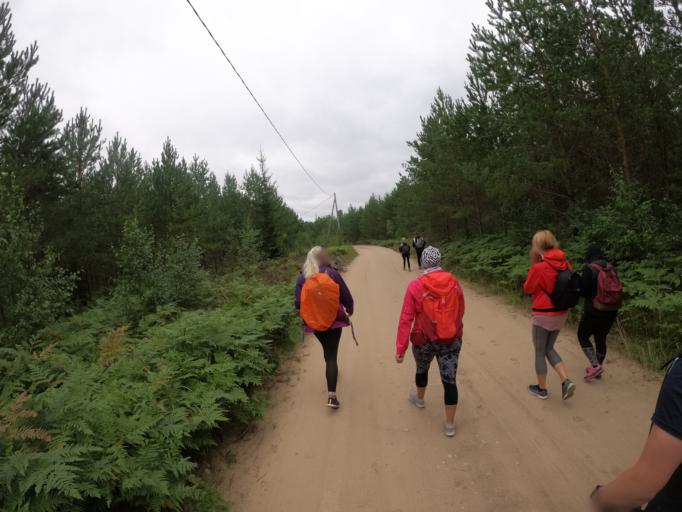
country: LV
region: Kuldigas Rajons
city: Kuldiga
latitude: 57.0200
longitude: 22.0032
